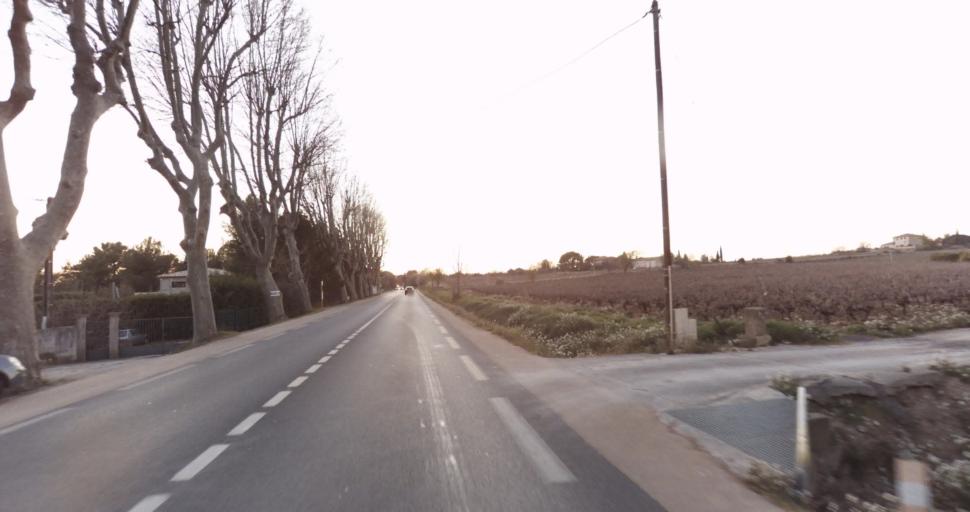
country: FR
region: Provence-Alpes-Cote d'Azur
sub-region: Departement des Bouches-du-Rhone
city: Aix-en-Provence
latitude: 43.5357
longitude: 5.4045
